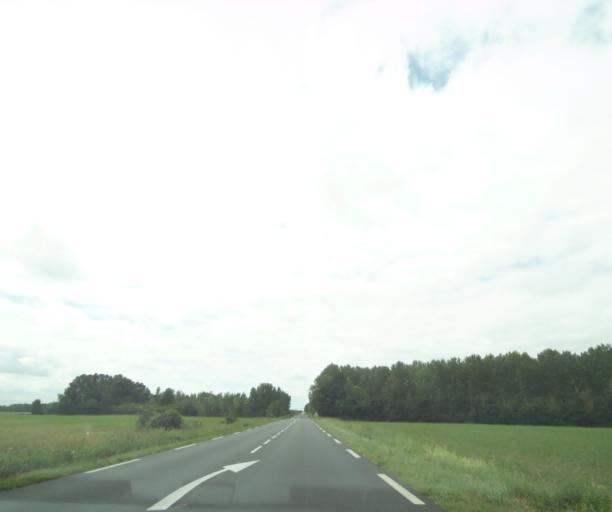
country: FR
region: Pays de la Loire
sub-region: Departement de Maine-et-Loire
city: Montreuil-Bellay
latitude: 47.1096
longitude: -0.1644
